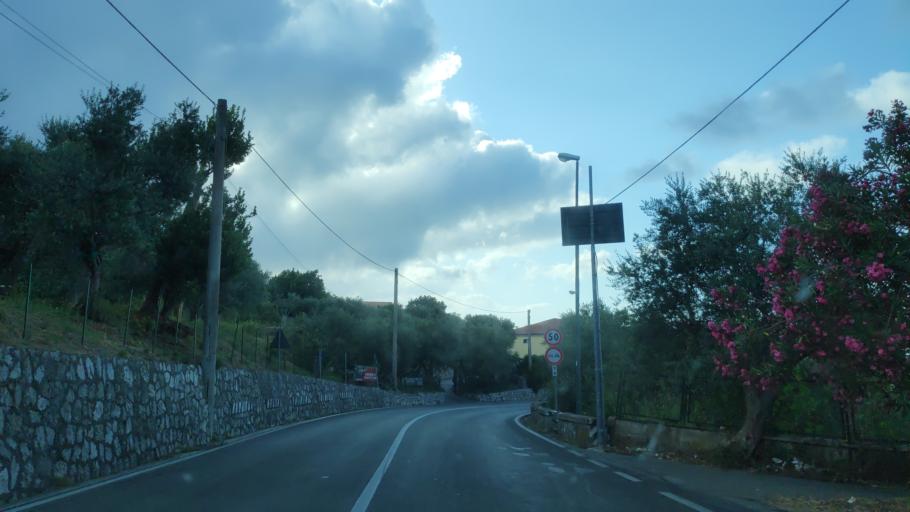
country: IT
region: Campania
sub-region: Provincia di Napoli
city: Piano di Sorrento
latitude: 40.6173
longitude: 14.4285
